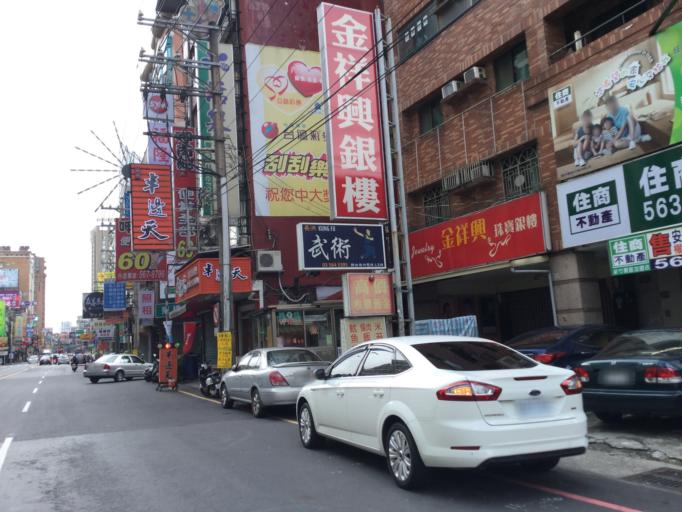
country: TW
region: Taiwan
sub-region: Hsinchu
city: Hsinchu
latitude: 24.7839
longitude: 121.0165
